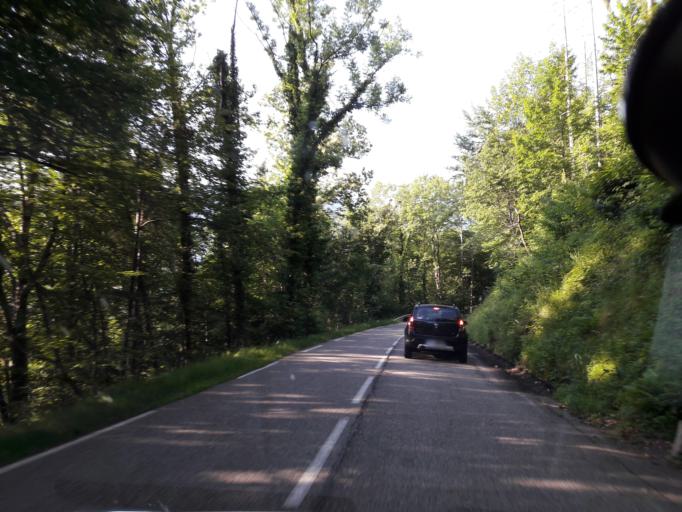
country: FR
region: Rhone-Alpes
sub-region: Departement de l'Isere
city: Vaulnaveys-le-Bas
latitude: 45.0360
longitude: 5.8290
